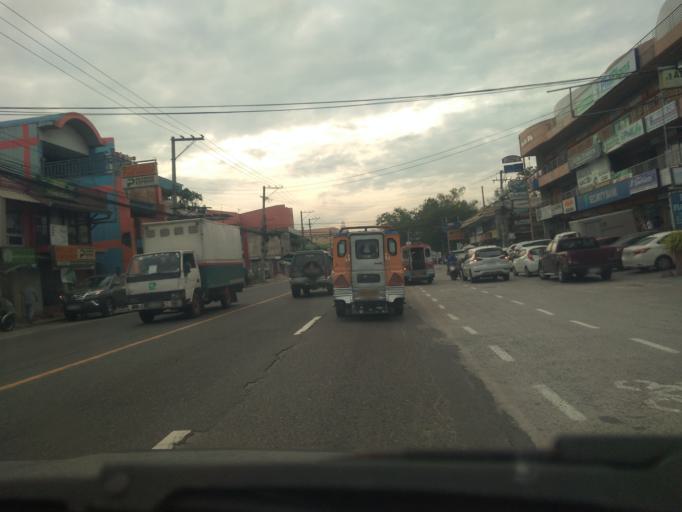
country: PH
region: Central Luzon
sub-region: Province of Pampanga
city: San Fernando
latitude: 15.0360
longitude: 120.6837
